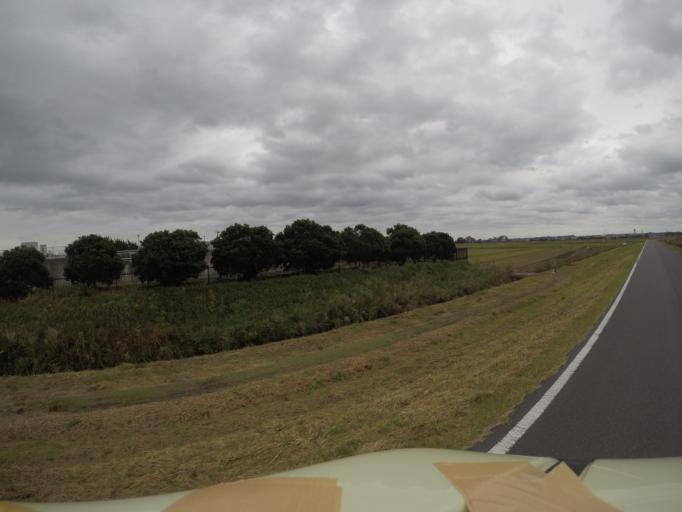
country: JP
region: Ibaraki
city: Inashiki
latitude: 36.0784
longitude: 140.3858
